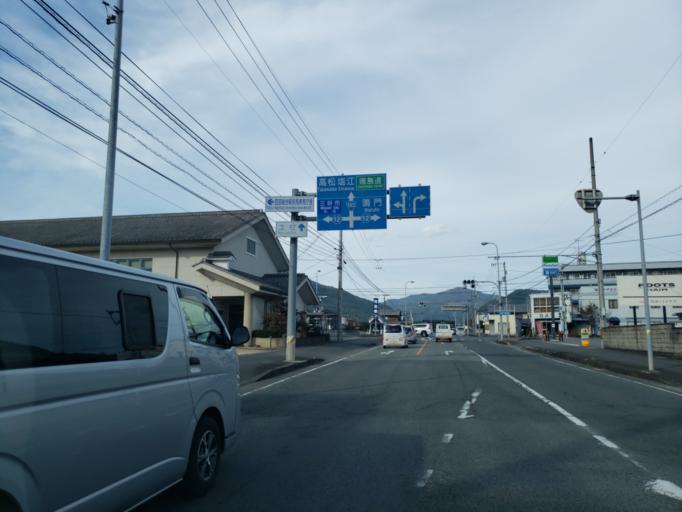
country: JP
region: Tokushima
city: Wakimachi
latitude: 34.0652
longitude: 134.1695
